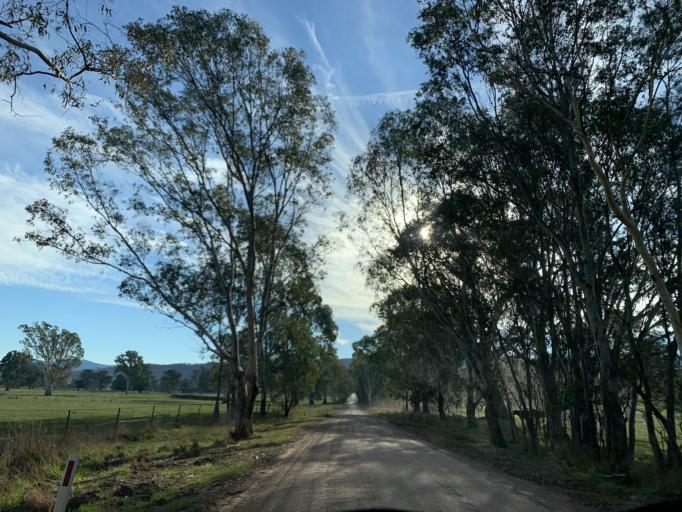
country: AU
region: Victoria
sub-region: Mansfield
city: Mansfield
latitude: -36.9635
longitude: 146.1083
